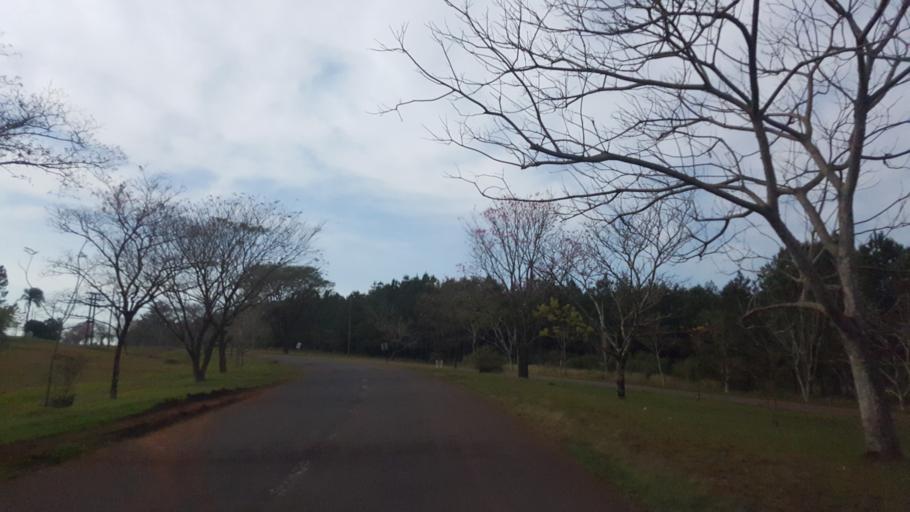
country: AR
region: Misiones
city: Capiovi
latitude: -26.9330
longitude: -55.1157
